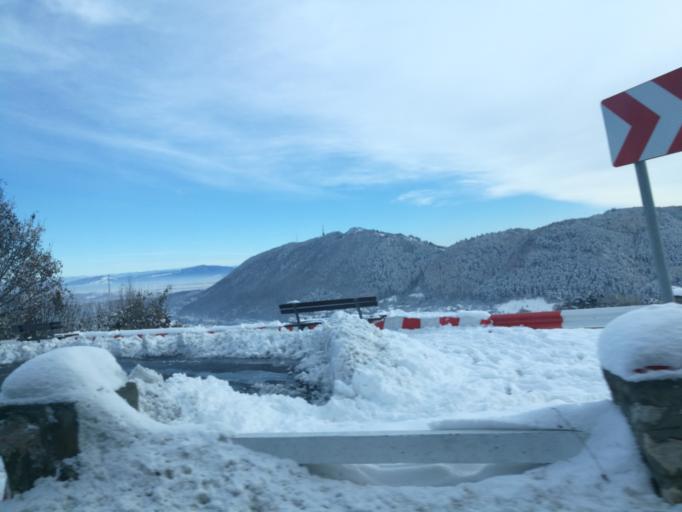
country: RO
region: Brasov
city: Brasov
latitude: 45.6338
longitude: 25.5647
